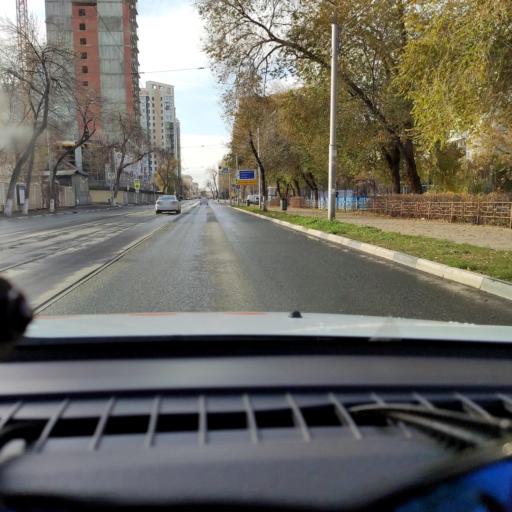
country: RU
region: Samara
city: Samara
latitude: 53.2052
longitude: 50.1203
